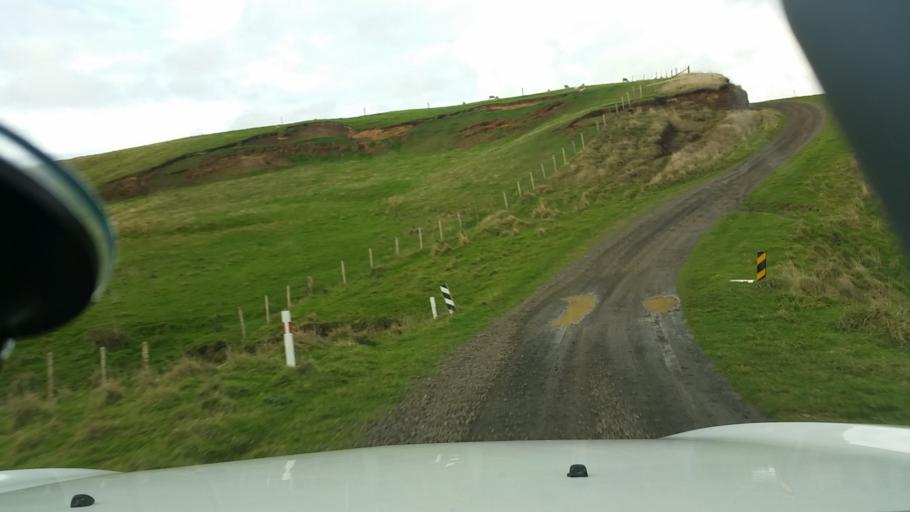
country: NZ
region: Chatham Islands
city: Waitangi
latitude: -44.0352
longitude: -176.6563
